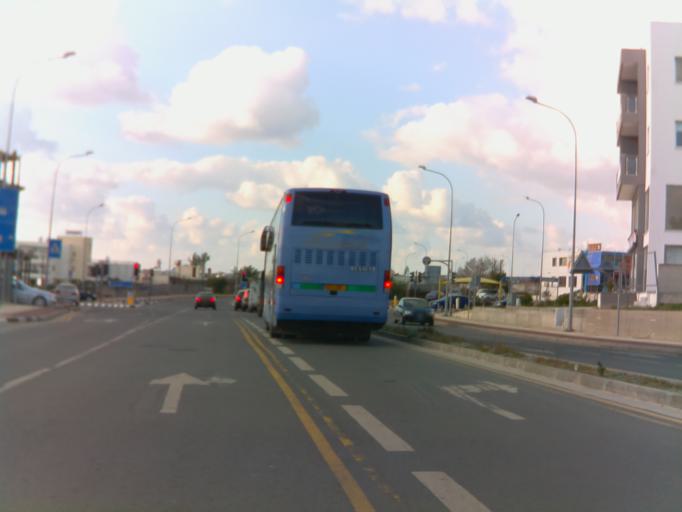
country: CY
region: Pafos
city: Paphos
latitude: 34.7918
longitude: 32.4366
